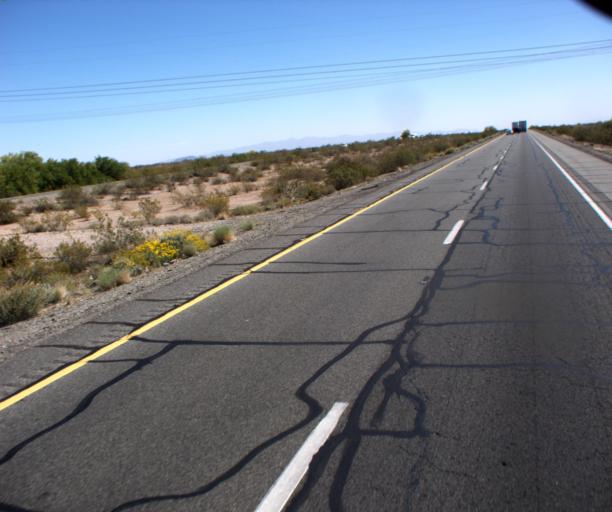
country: US
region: Arizona
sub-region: Maricopa County
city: Buckeye
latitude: 33.5140
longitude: -113.0328
